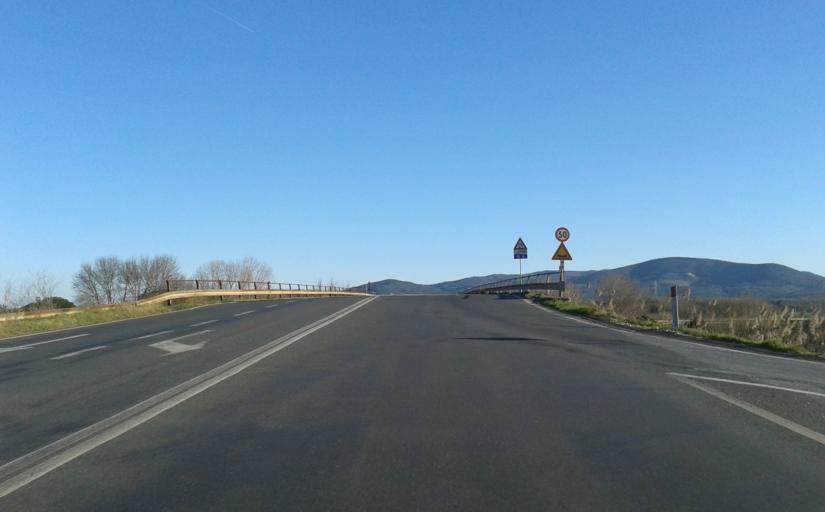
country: IT
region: Tuscany
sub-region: Provincia di Livorno
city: Livorno
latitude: 43.5745
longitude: 10.3456
